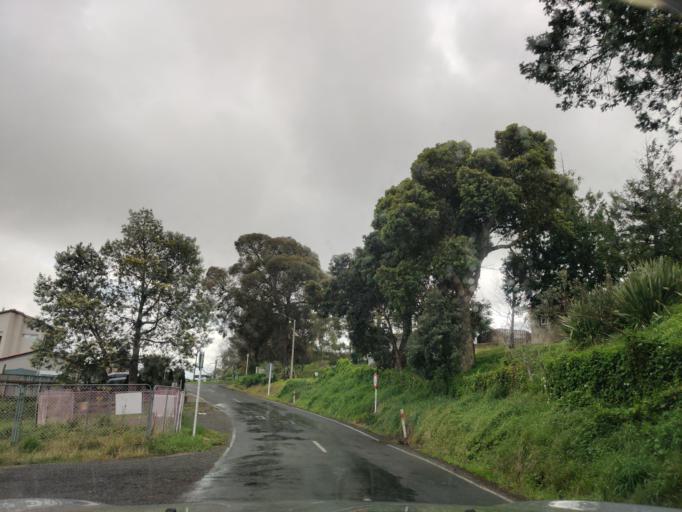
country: NZ
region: Hawke's Bay
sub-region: Hastings District
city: Hastings
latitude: -39.6767
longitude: 176.8959
